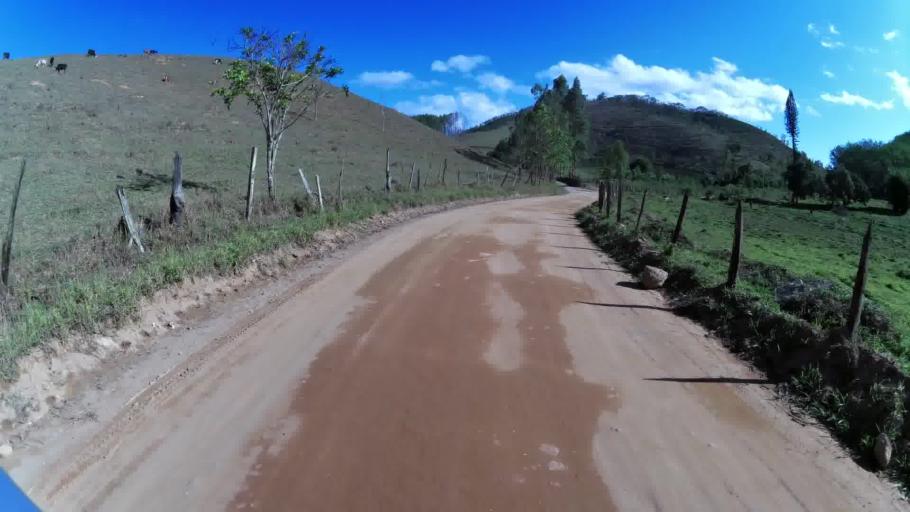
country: BR
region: Espirito Santo
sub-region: Sao Jose Do Calcado
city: Sao Jose do Calcado
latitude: -21.0222
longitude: -41.5684
